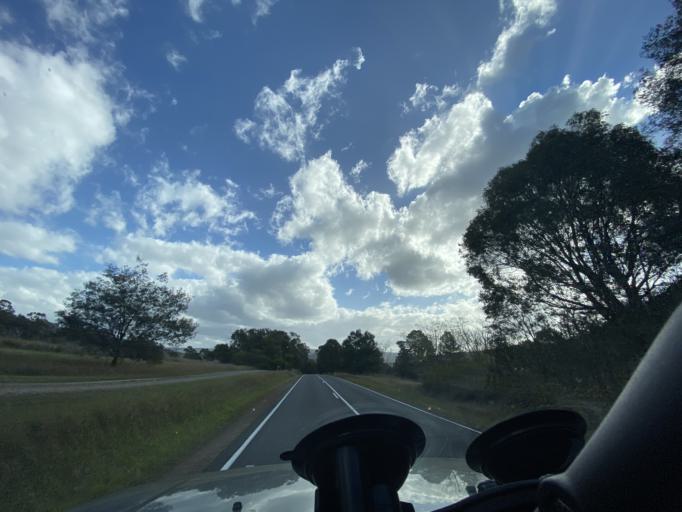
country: AU
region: Victoria
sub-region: Murrindindi
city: Kinglake West
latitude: -37.3223
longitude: 145.3118
